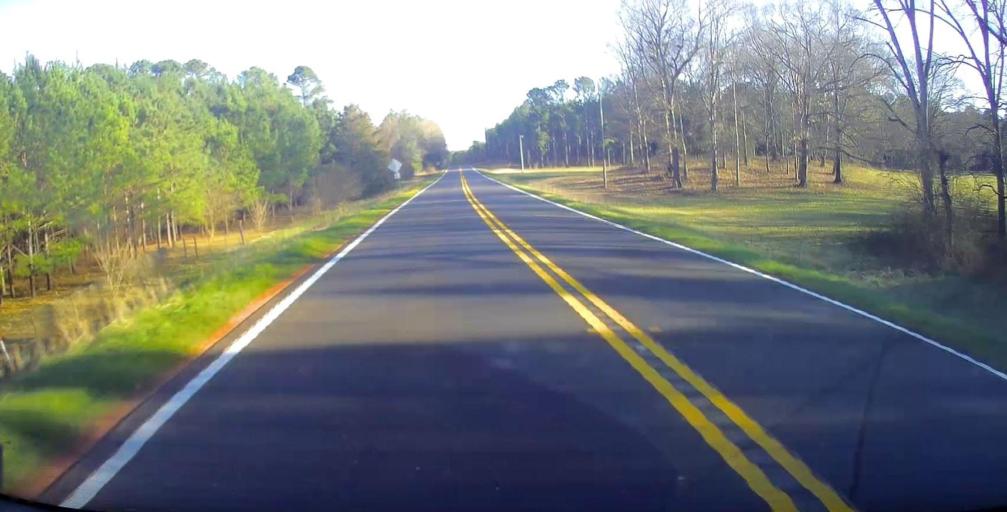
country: US
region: Georgia
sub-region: Meriwether County
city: Manchester
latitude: 32.9048
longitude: -84.7202
